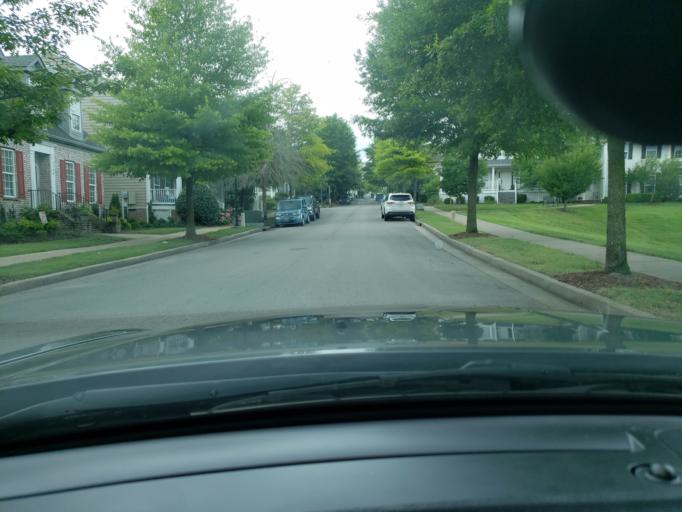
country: US
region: Tennessee
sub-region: Williamson County
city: Brentwood Estates
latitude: 36.0244
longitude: -86.7086
